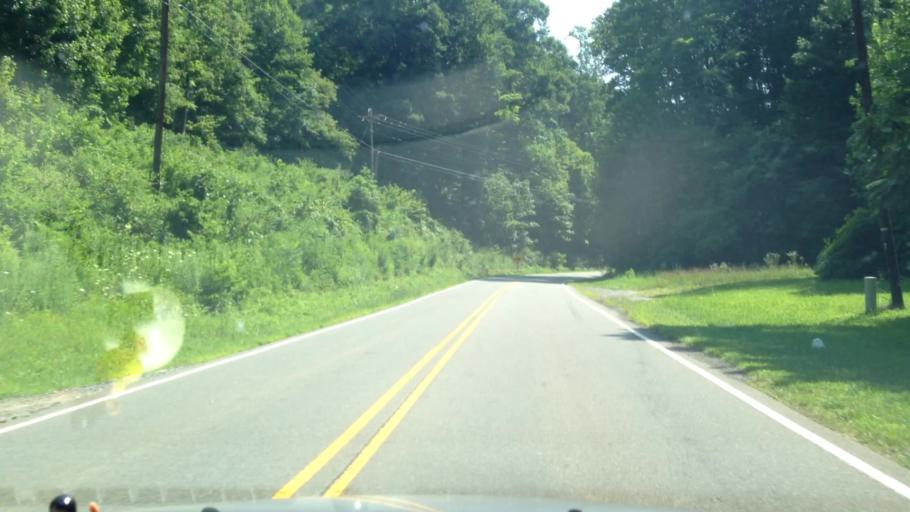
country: US
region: North Carolina
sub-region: Surry County
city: Flat Rock
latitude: 36.5362
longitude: -80.5191
